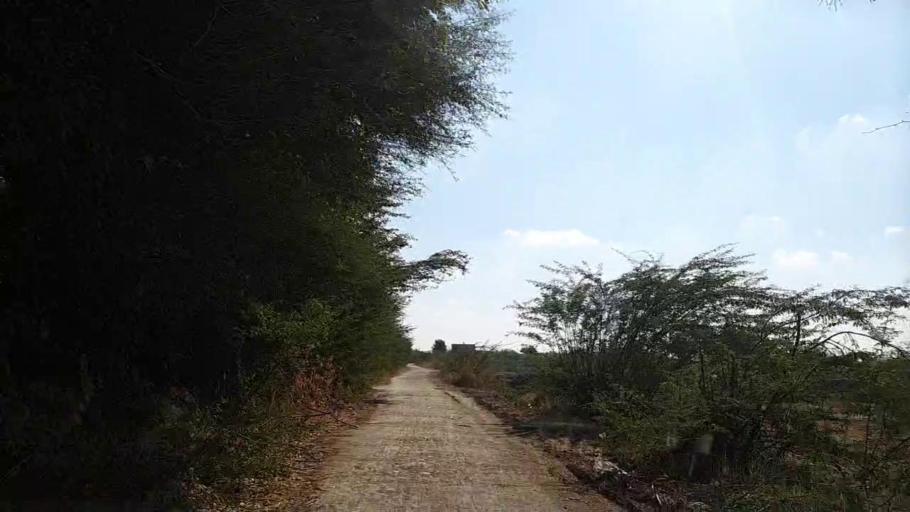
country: PK
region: Sindh
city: Pithoro
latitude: 25.6421
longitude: 69.4475
